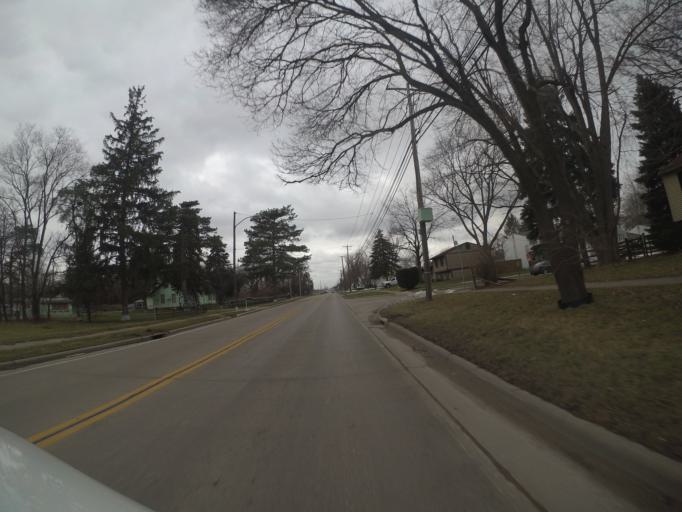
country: US
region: Ohio
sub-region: Wood County
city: Rossford
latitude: 41.6090
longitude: -83.5312
